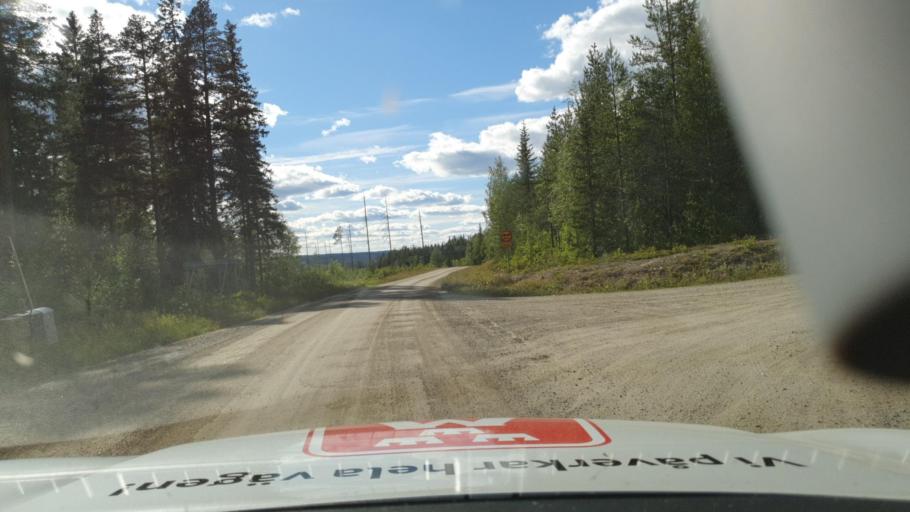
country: SE
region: Vaesterbotten
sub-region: Lycksele Kommun
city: Lycksele
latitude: 64.4055
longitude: 18.5401
